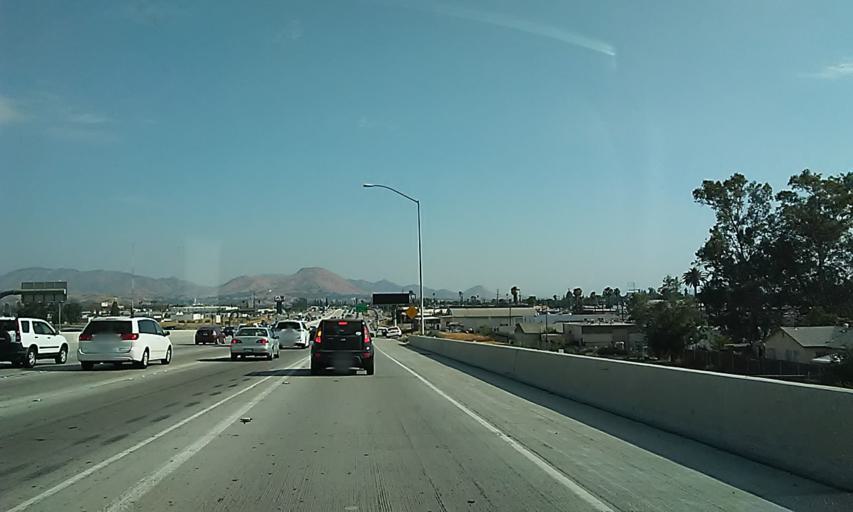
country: US
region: California
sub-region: San Bernardino County
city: San Bernardino
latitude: 34.0993
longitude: -117.3022
